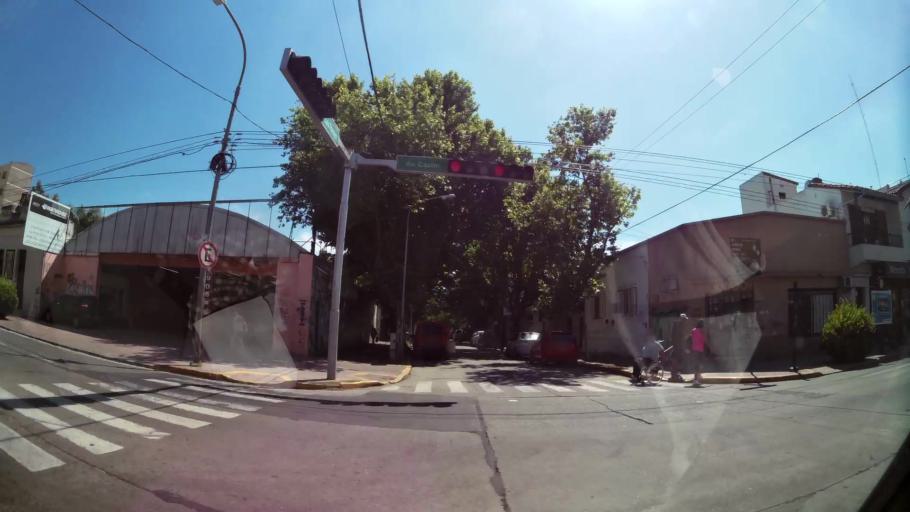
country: AR
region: Buenos Aires
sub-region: Partido de Tigre
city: Tigre
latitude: -34.4284
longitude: -58.5733
